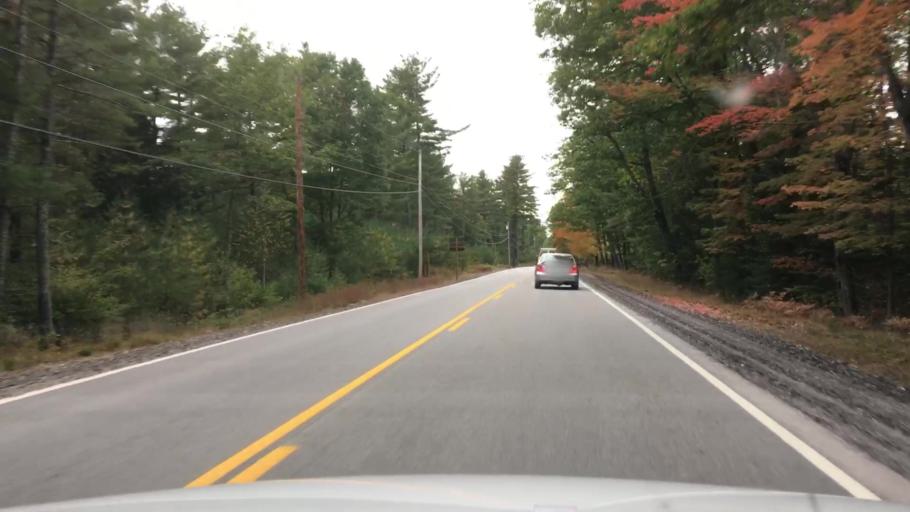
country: US
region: Maine
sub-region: Cumberland County
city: Harrison
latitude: 44.2143
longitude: -70.6830
